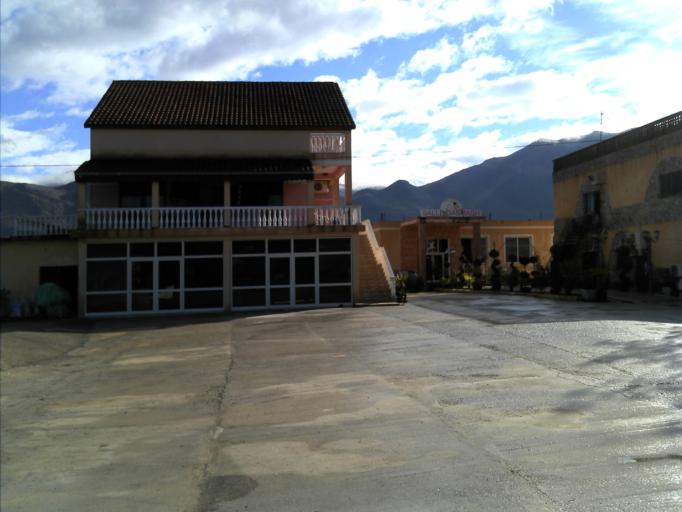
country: AL
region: Shkoder
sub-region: Rrethi i Malesia e Madhe
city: Hot
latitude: 42.3066
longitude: 19.4407
